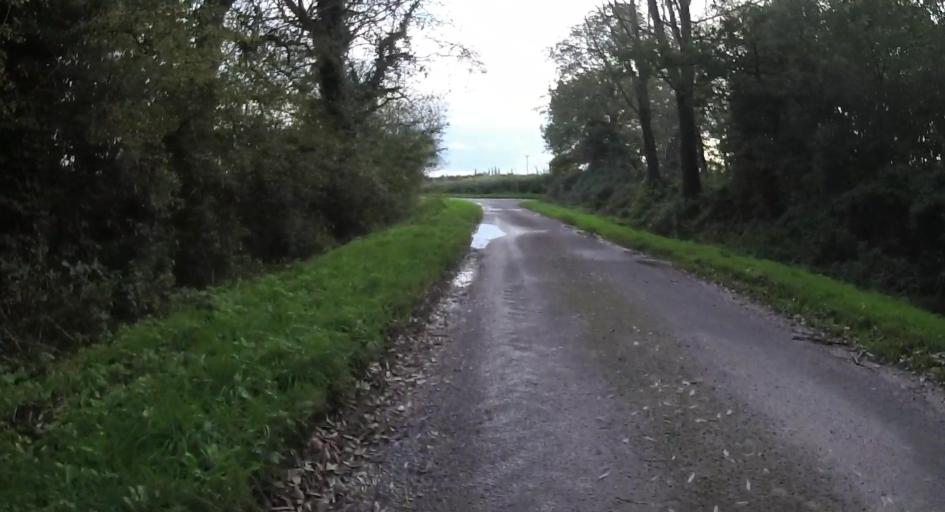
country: GB
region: England
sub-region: Wokingham
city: Swallowfield
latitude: 51.3737
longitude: -0.9610
